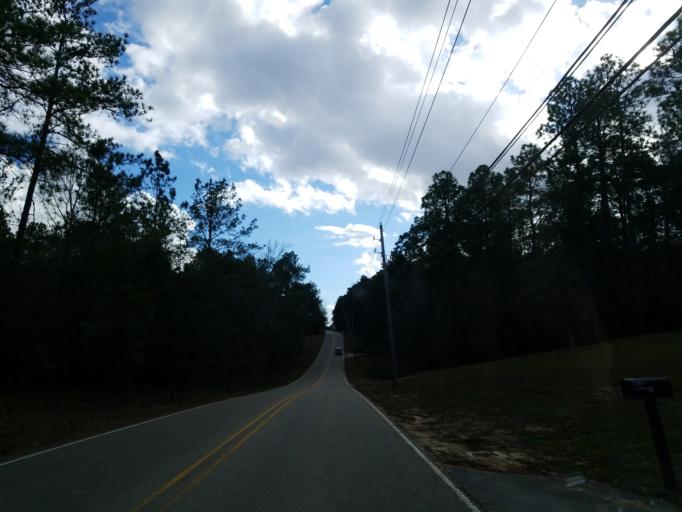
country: US
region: Mississippi
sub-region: Lamar County
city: West Hattiesburg
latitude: 31.2957
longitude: -89.3480
